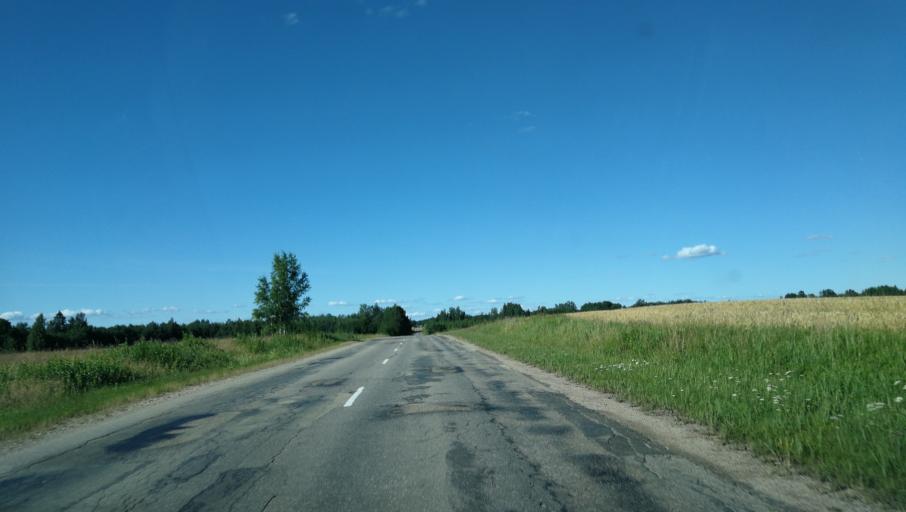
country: LV
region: Madonas Rajons
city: Madona
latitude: 56.9506
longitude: 26.0411
